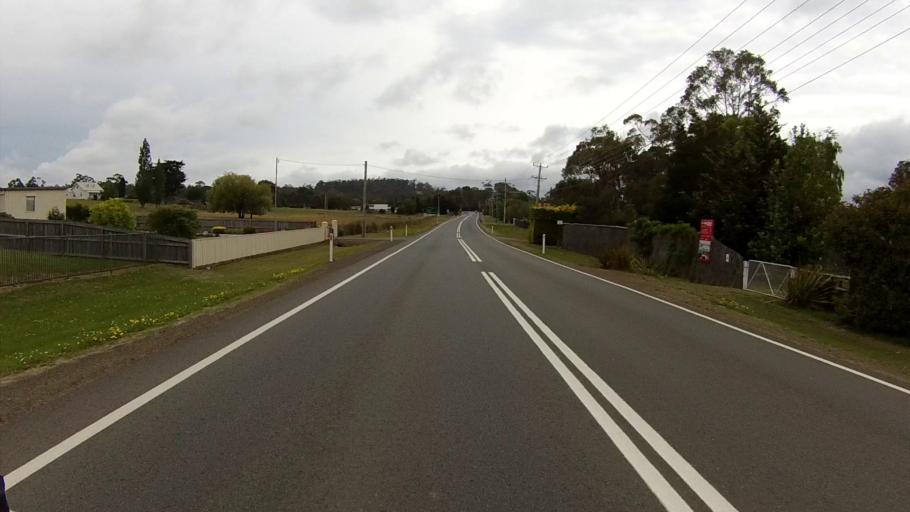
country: AU
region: Tasmania
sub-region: Sorell
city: Sorell
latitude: -42.5517
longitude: 147.8780
